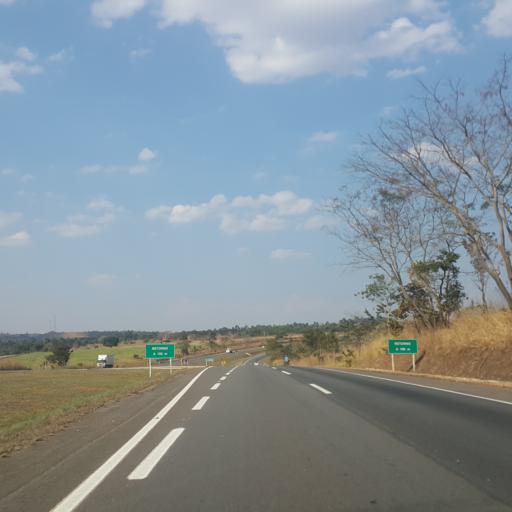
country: BR
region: Goias
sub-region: Abadiania
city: Abadiania
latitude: -16.1153
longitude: -48.5490
